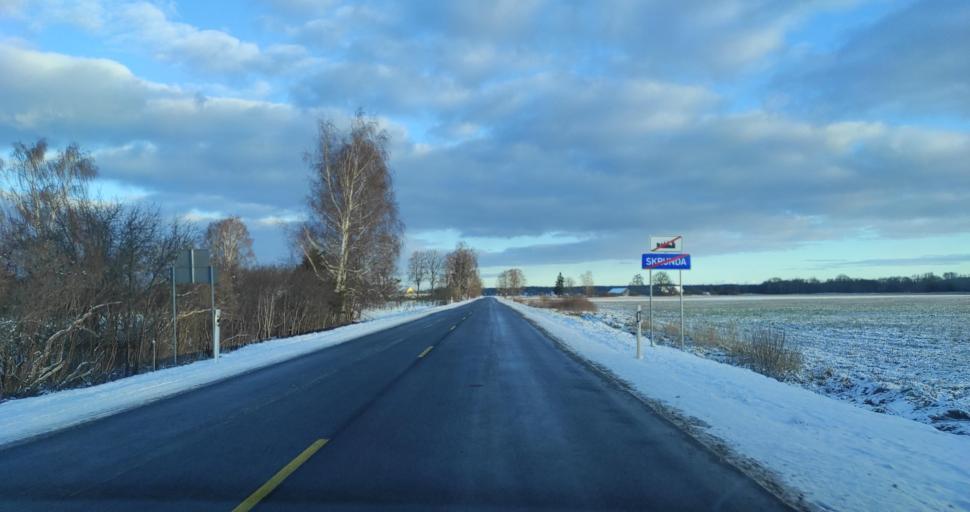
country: LV
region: Skrunda
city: Skrunda
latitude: 56.6857
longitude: 22.0181
